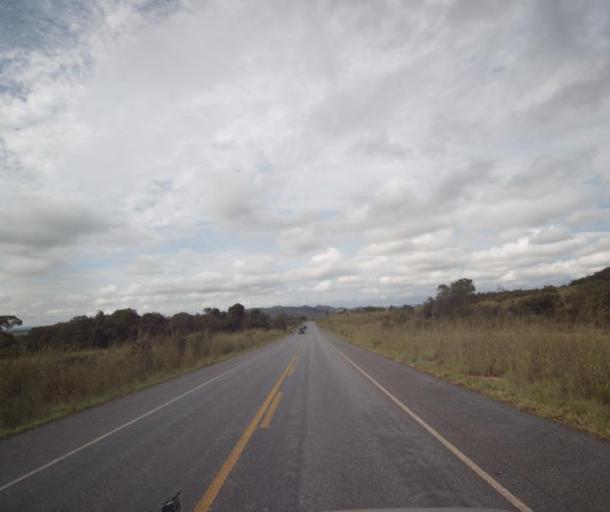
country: BR
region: Goias
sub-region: Pirenopolis
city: Pirenopolis
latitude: -15.5465
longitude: -48.6228
